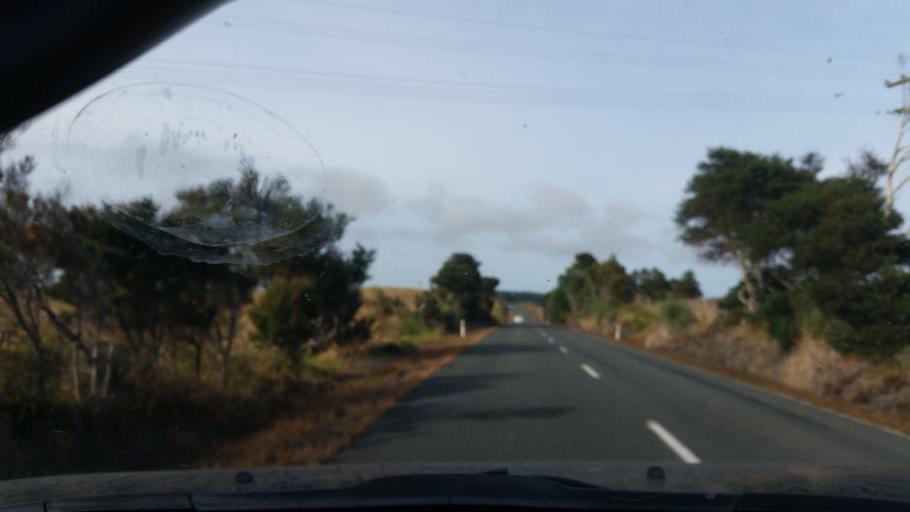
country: NZ
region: Northland
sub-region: Kaipara District
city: Dargaville
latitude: -36.2008
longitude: 174.0476
